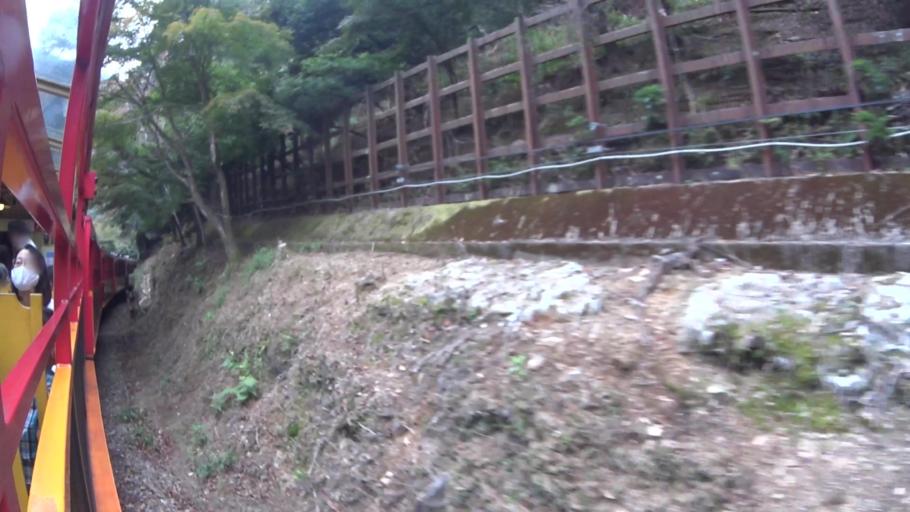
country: JP
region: Kyoto
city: Muko
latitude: 35.0180
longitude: 135.6597
